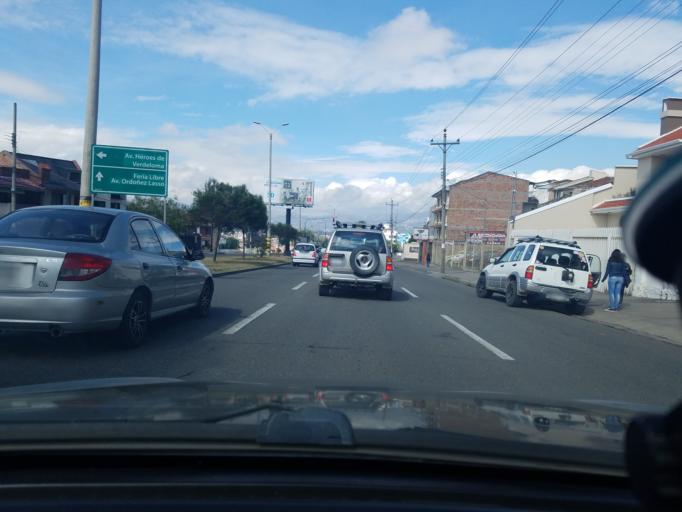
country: EC
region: Azuay
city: Cuenca
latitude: -2.8868
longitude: -79.0093
